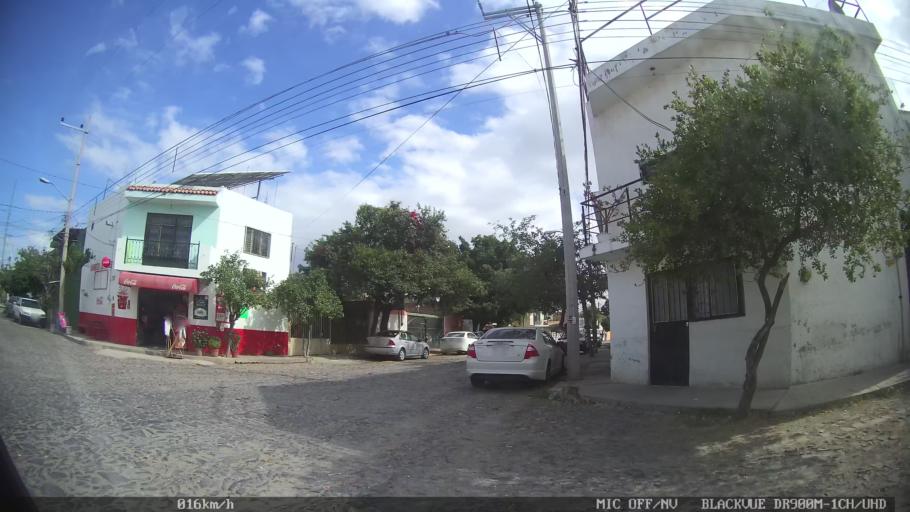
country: MX
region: Jalisco
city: Tlaquepaque
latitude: 20.6821
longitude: -103.2562
